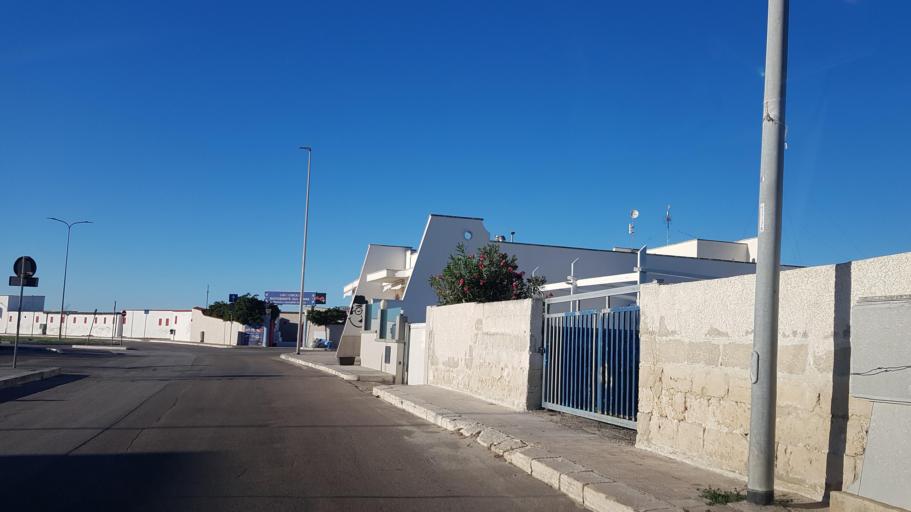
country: IT
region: Apulia
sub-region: Provincia di Lecce
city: Giorgilorio
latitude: 40.4669
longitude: 18.1949
